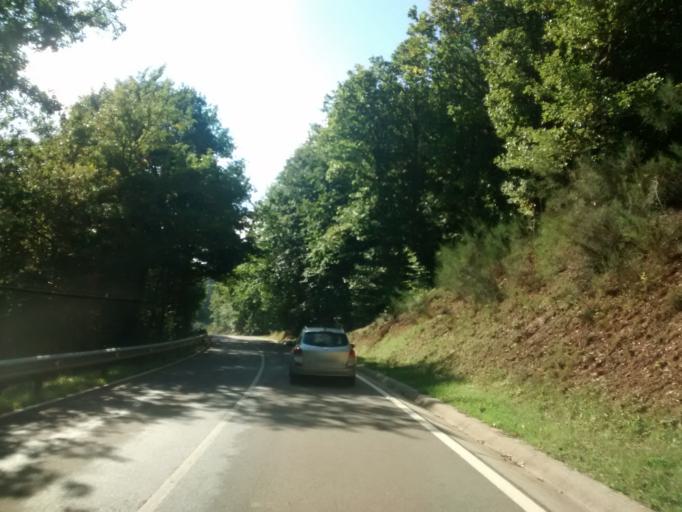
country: ES
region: Cantabria
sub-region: Provincia de Cantabria
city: Reinosa
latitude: 42.9481
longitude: -4.0534
